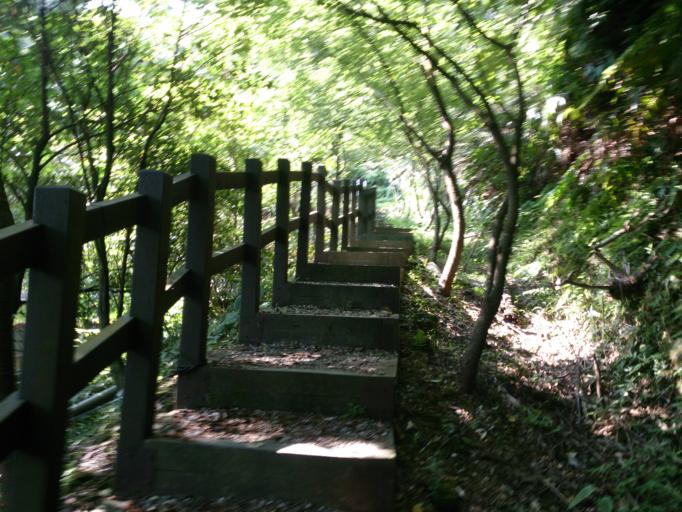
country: TW
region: Taiwan
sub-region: Keelung
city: Keelung
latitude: 25.1235
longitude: 121.7098
